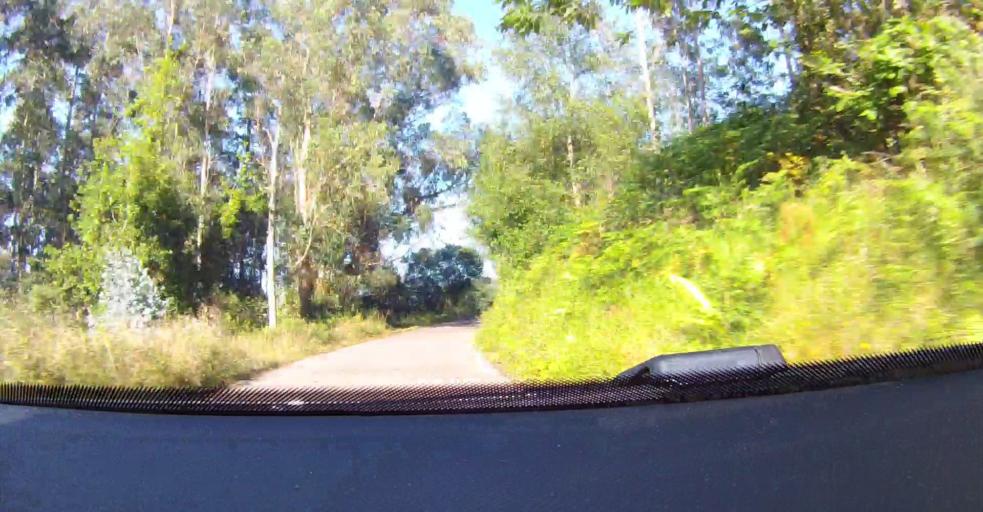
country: ES
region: Asturias
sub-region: Province of Asturias
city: Villaviciosa
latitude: 43.4859
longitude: -5.3991
